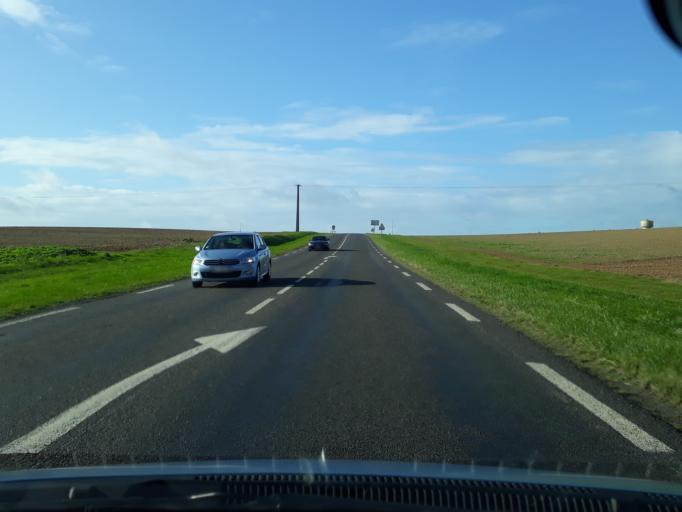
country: FR
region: Centre
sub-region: Departement du Loiret
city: Malesherbes
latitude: 48.2745
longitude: 2.3804
